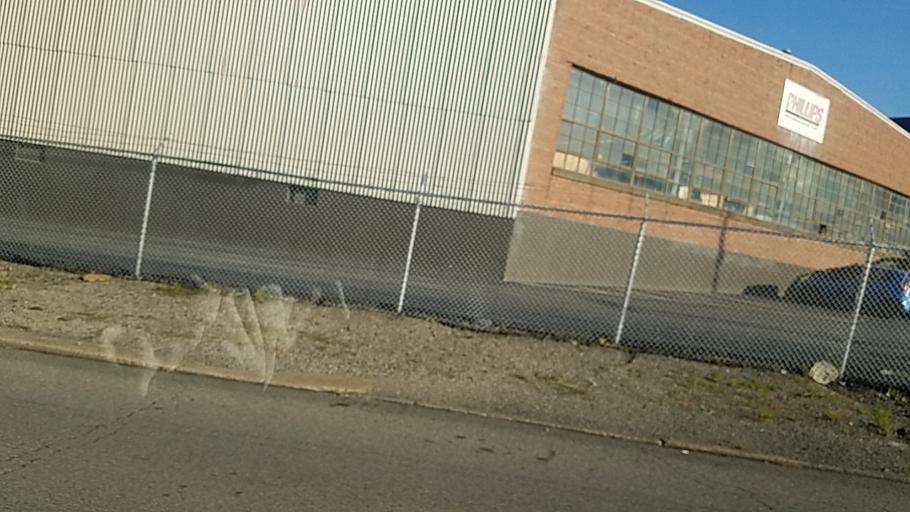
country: US
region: Ohio
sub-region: Trumbull County
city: Niles
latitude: 41.1753
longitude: -80.7522
